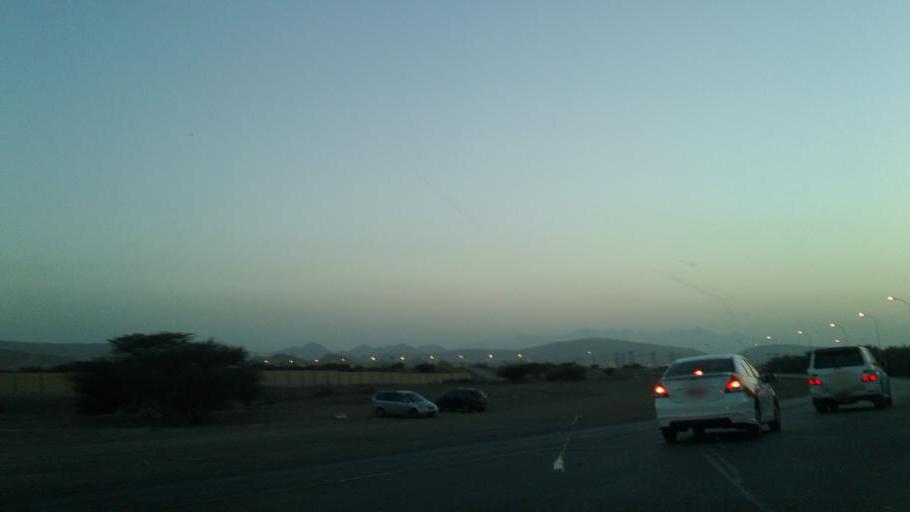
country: OM
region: Muhafazat Masqat
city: As Sib al Jadidah
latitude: 23.5899
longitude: 58.2173
